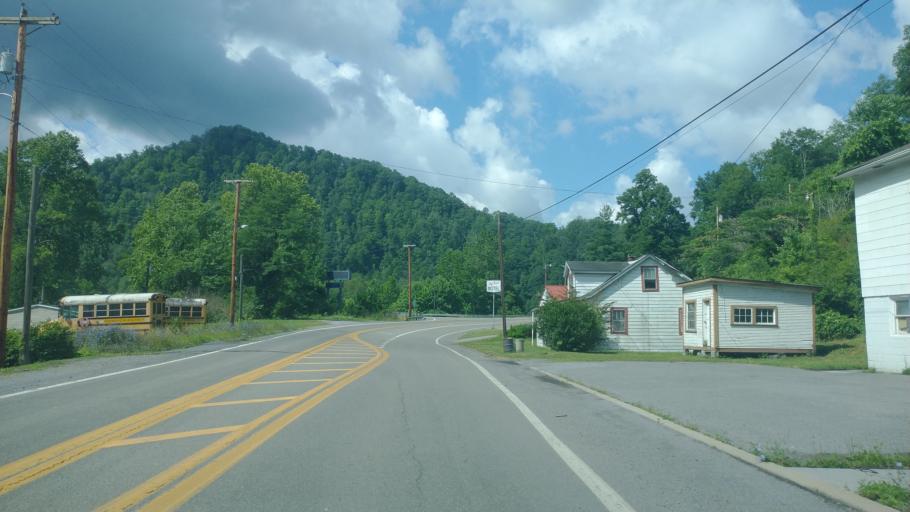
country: US
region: West Virginia
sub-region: McDowell County
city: Welch
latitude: 37.4149
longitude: -81.5210
